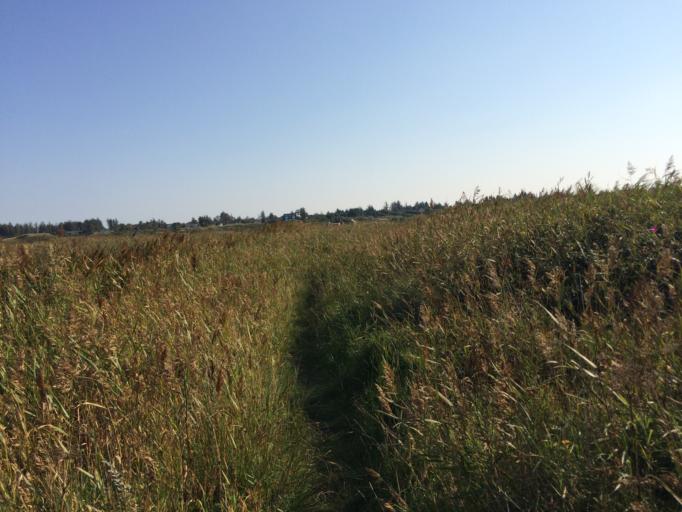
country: DK
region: Central Jutland
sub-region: Holstebro Kommune
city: Ulfborg
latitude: 56.3338
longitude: 8.1462
